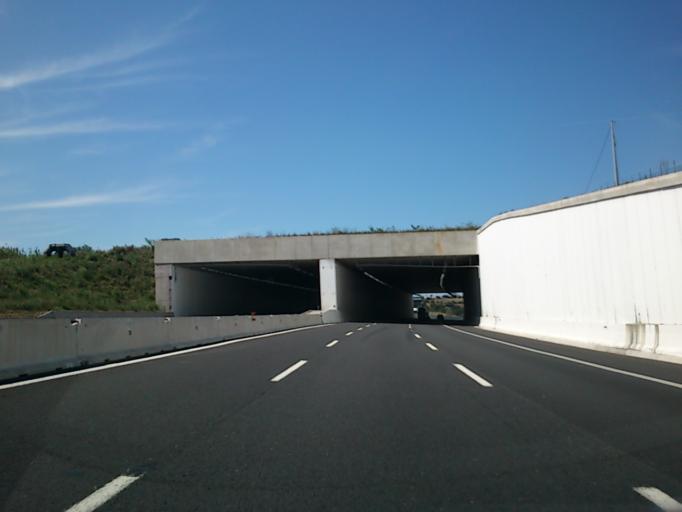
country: IT
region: The Marches
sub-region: Provincia di Pesaro e Urbino
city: Villa Ceccolini
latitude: 43.8993
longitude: 12.8376
